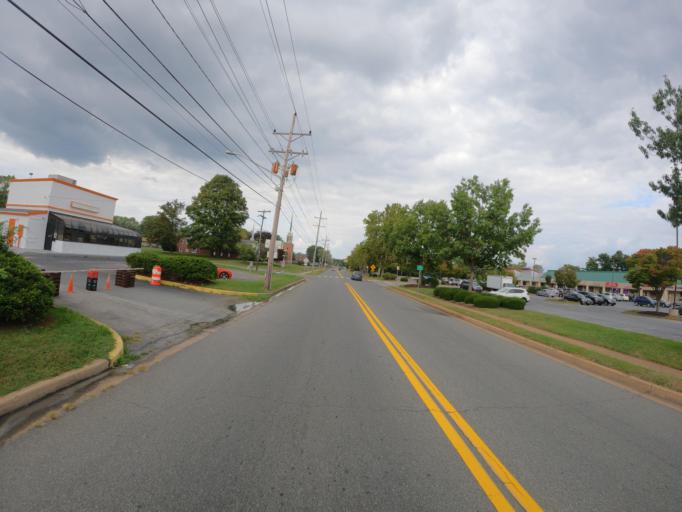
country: US
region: Delaware
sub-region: New Castle County
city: Brookside
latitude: 39.6649
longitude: -75.7269
